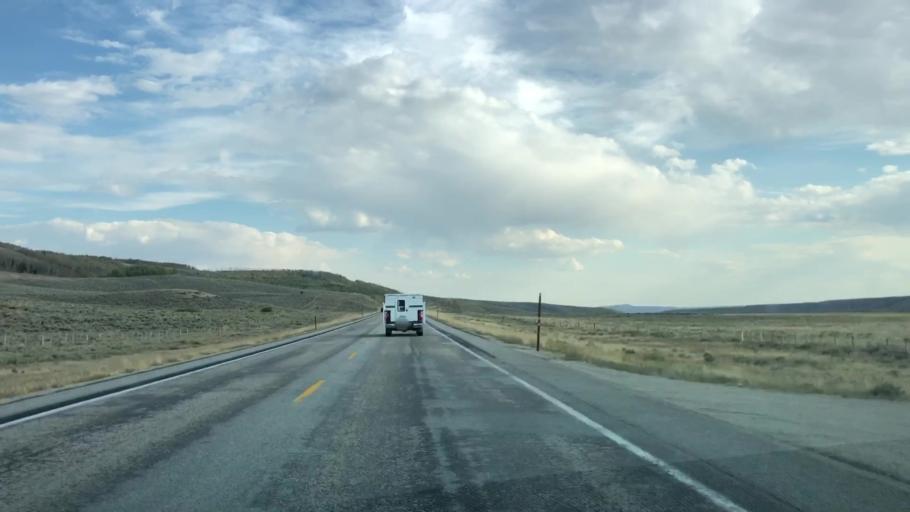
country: US
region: Wyoming
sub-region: Sublette County
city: Pinedale
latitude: 43.0978
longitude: -110.1679
